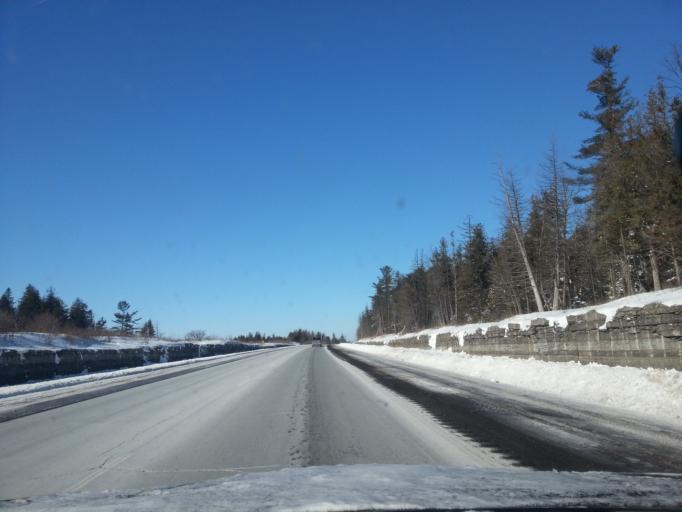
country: CA
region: Ontario
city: Arnprior
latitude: 45.3391
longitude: -76.1865
